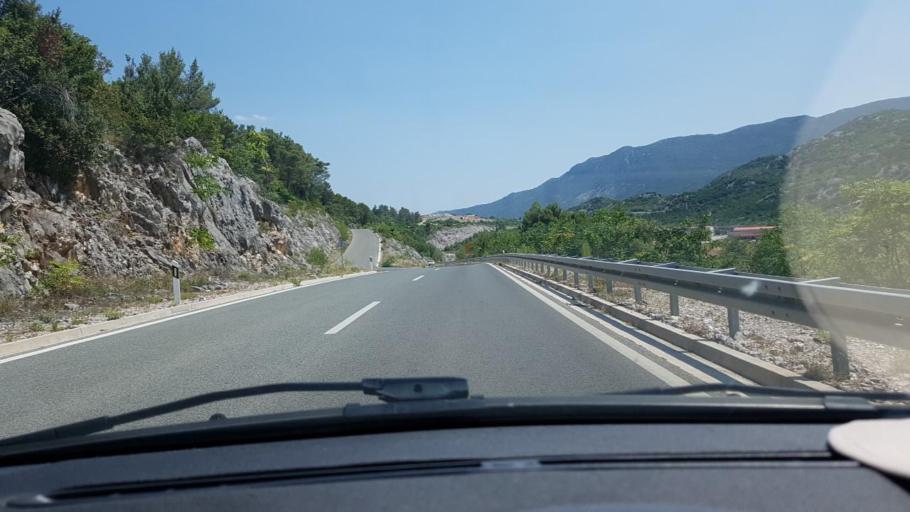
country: HR
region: Splitsko-Dalmatinska
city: Vrgorac
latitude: 43.1968
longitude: 17.3774
